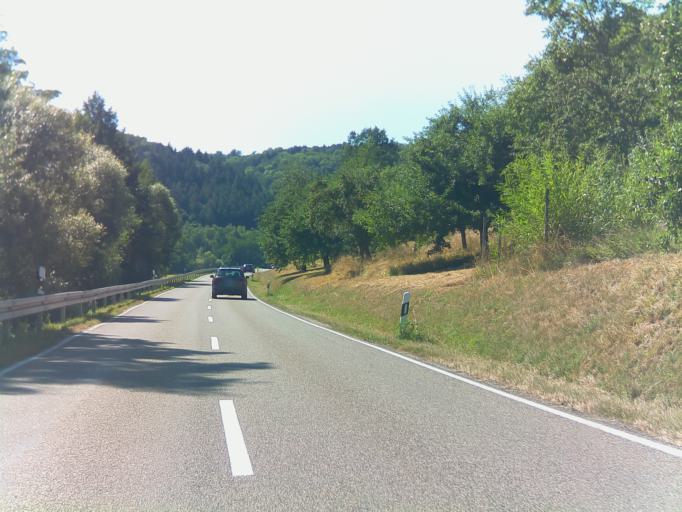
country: DE
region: Baden-Wuerttemberg
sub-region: Regierungsbezirk Stuttgart
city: Wertheim
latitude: 49.7310
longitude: 9.5271
